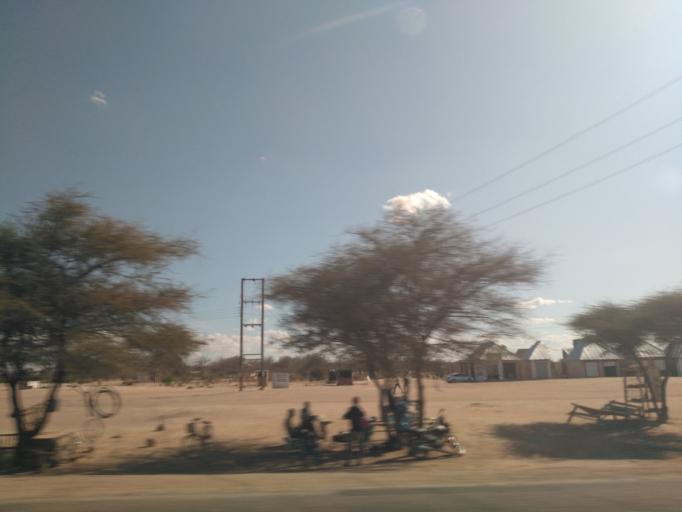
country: TZ
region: Dodoma
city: Dodoma
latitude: -6.1435
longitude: 35.6971
